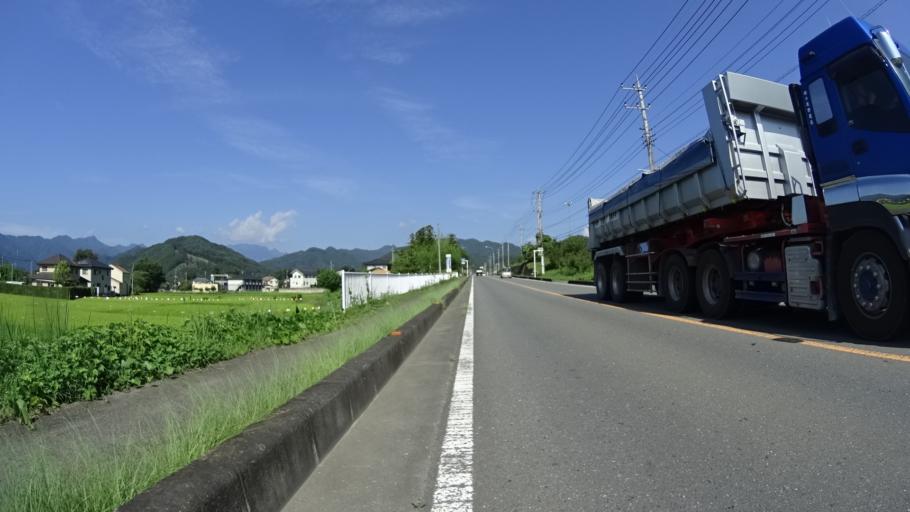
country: JP
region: Saitama
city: Chichibu
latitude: 36.0270
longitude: 138.9947
